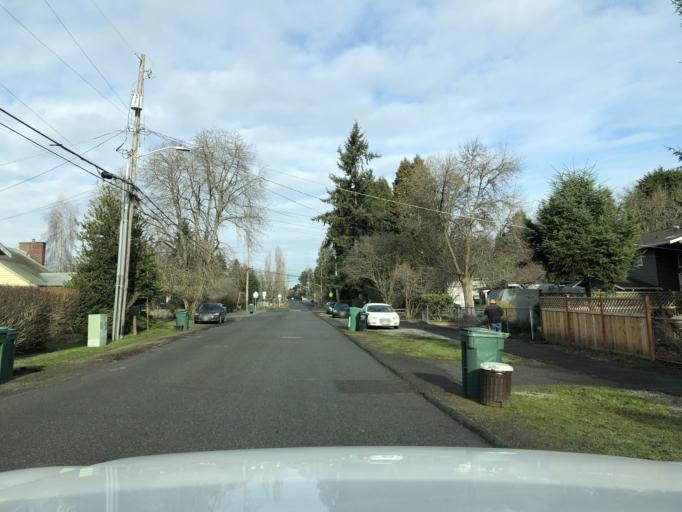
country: US
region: Washington
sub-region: King County
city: Lake Forest Park
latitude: 47.7255
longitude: -122.3074
